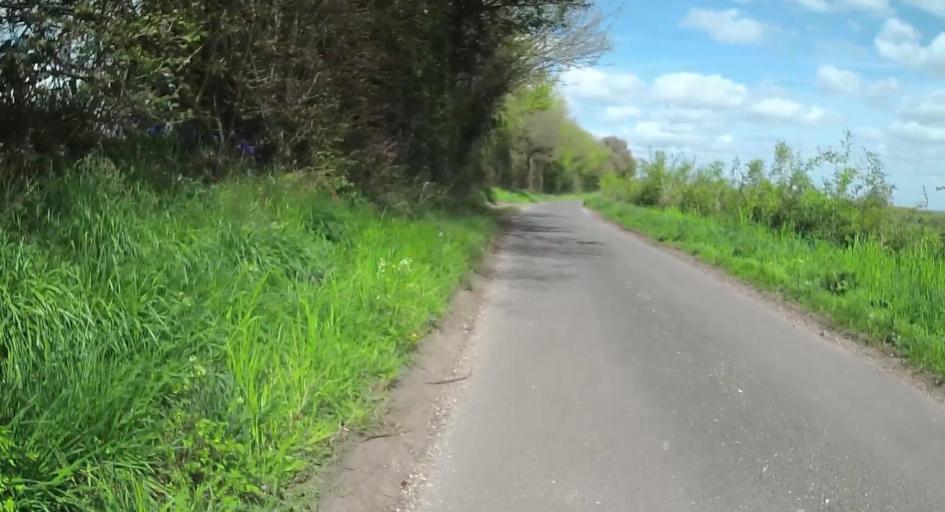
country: GB
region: England
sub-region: Hampshire
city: Romsey
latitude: 51.0583
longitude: -1.5328
